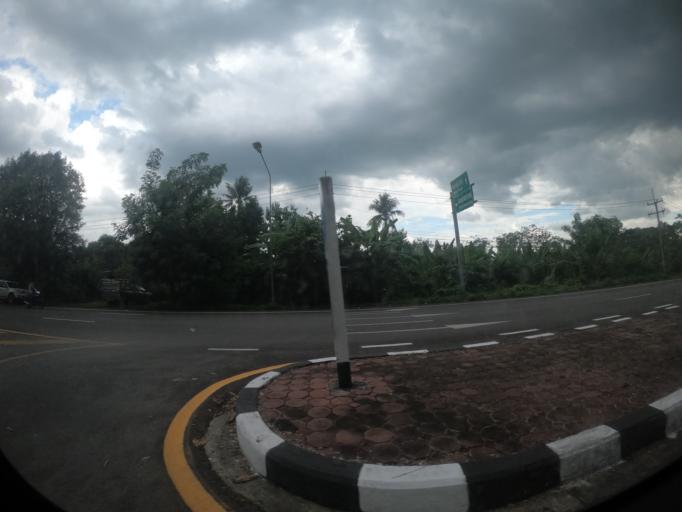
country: TH
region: Nakhon Nayok
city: Nakhon Nayok
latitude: 14.3231
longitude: 101.3131
